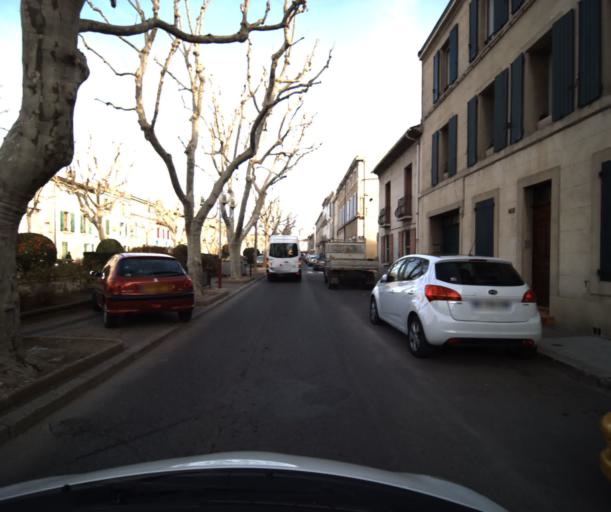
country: FR
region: Provence-Alpes-Cote d'Azur
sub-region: Departement du Vaucluse
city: Pertuis
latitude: 43.6898
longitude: 5.5000
